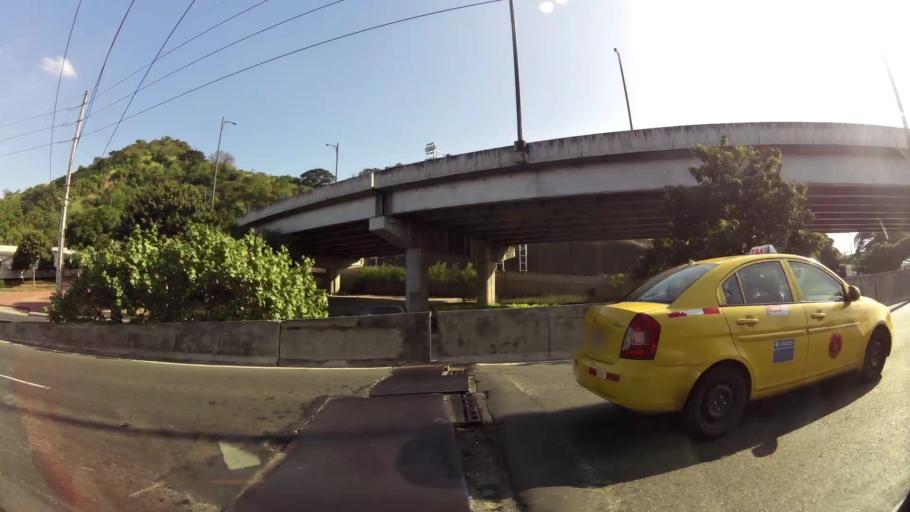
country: EC
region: Guayas
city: Guayaquil
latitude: -2.1628
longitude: -79.9265
